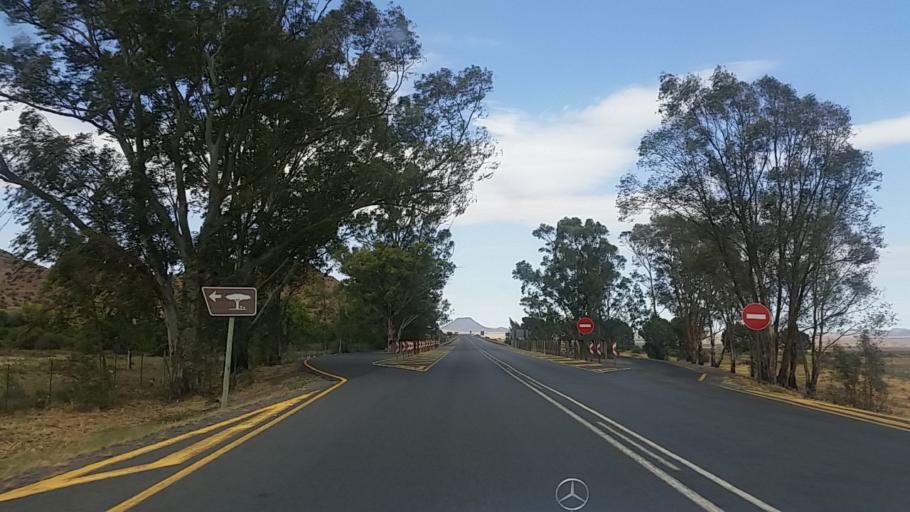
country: ZA
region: Northern Cape
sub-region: Pixley ka Seme District Municipality
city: Colesberg
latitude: -30.6470
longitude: 25.2114
